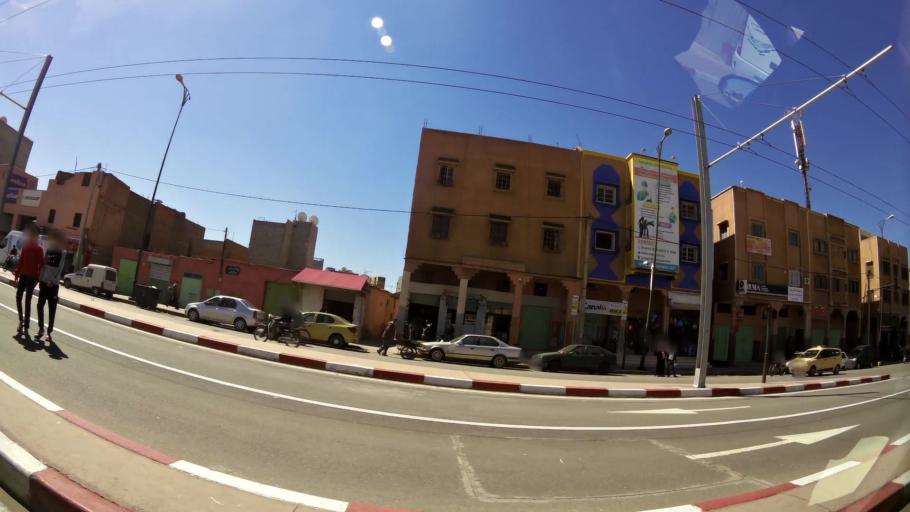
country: MA
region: Marrakech-Tensift-Al Haouz
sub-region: Marrakech
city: Marrakesh
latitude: 31.6277
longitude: -8.0624
